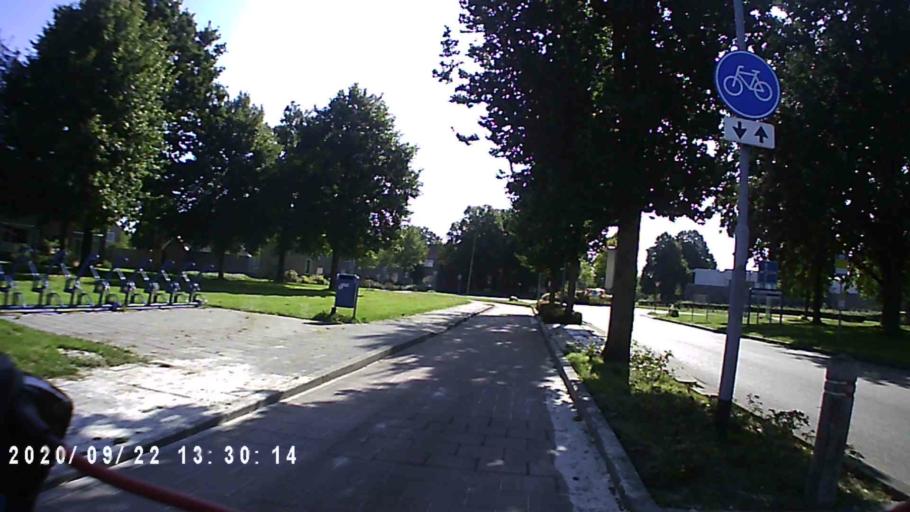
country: NL
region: Groningen
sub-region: Gemeente Leek
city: Leek
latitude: 53.1642
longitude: 6.3809
